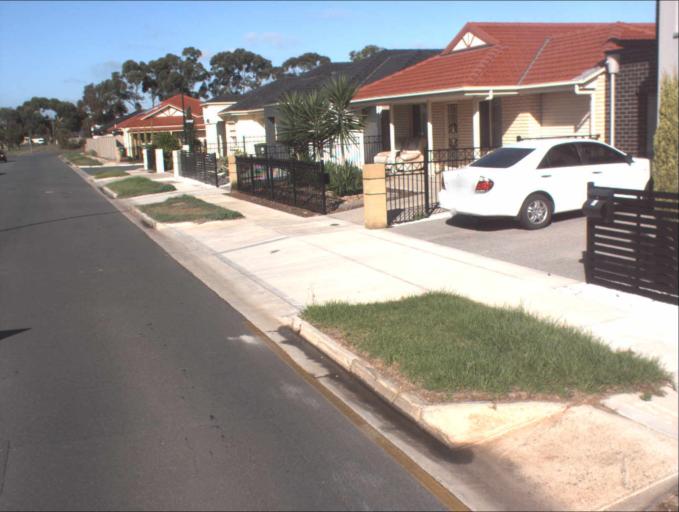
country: AU
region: South Australia
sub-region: Charles Sturt
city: Woodville North
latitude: -34.8550
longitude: 138.5503
